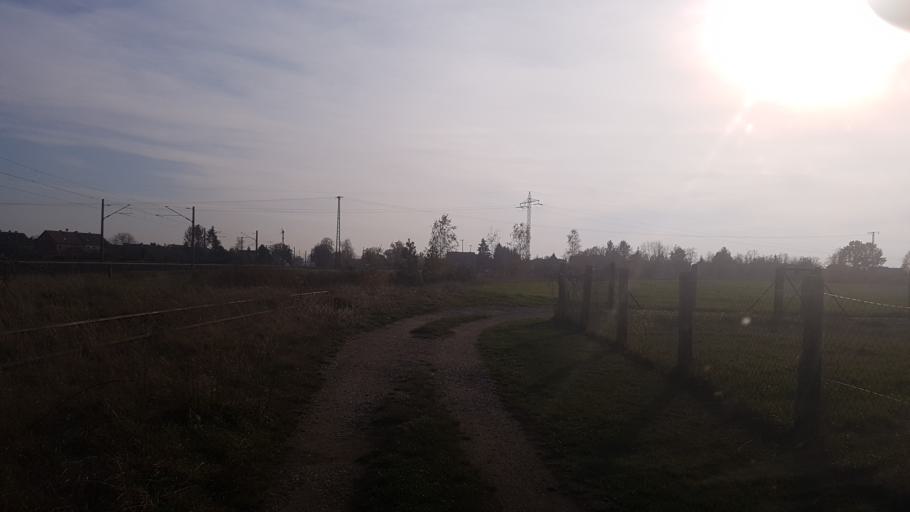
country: DE
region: Brandenburg
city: Falkenberg
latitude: 51.5772
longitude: 13.2500
